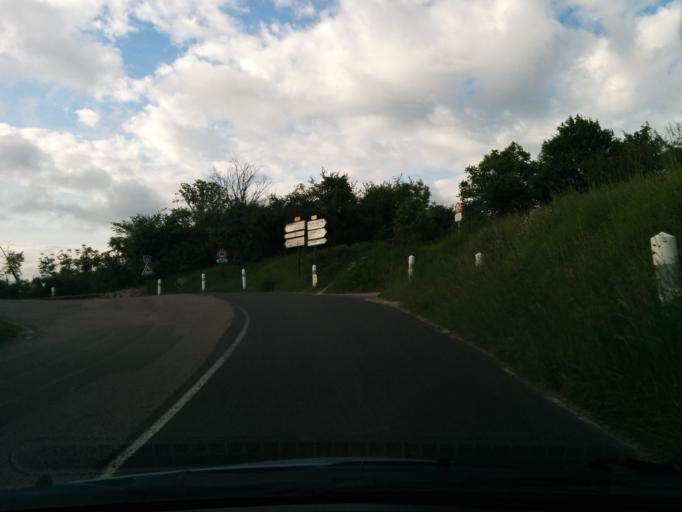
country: FR
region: Haute-Normandie
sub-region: Departement de l'Eure
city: Gasny
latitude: 49.0778
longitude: 1.6144
